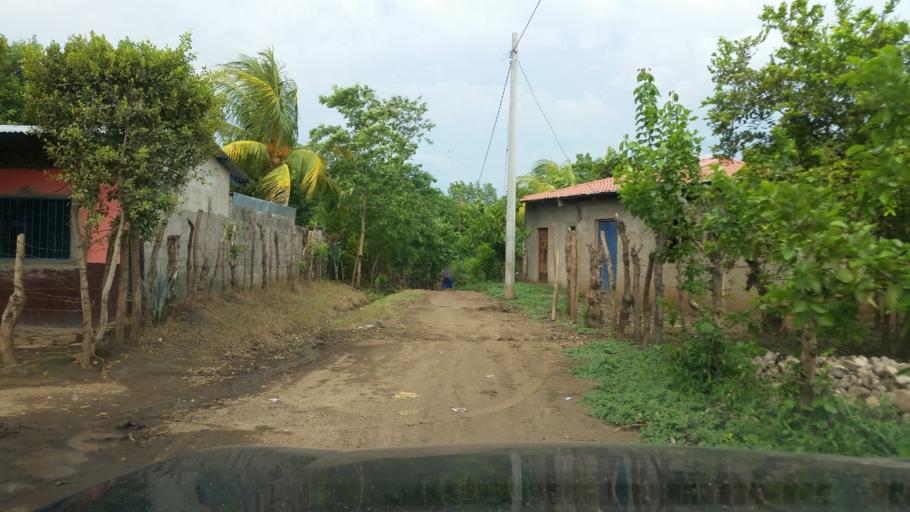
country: NI
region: Chinandega
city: Puerto Morazan
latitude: 12.7649
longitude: -87.1238
